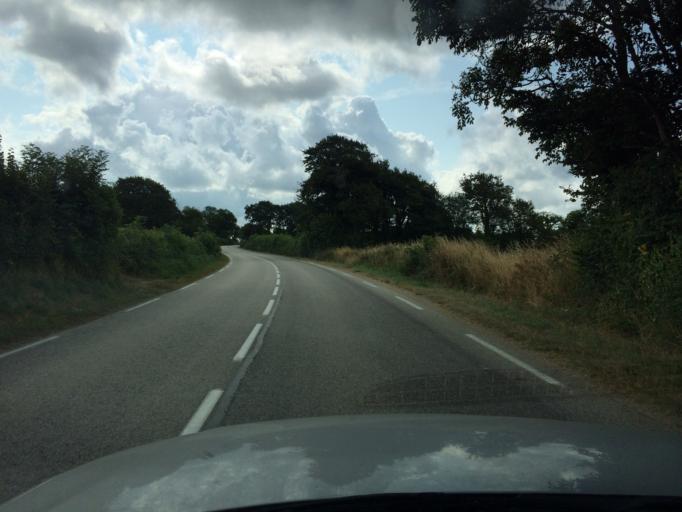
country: FR
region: Lower Normandy
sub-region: Departement de la Manche
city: Martinvast
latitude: 49.5703
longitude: -1.6988
